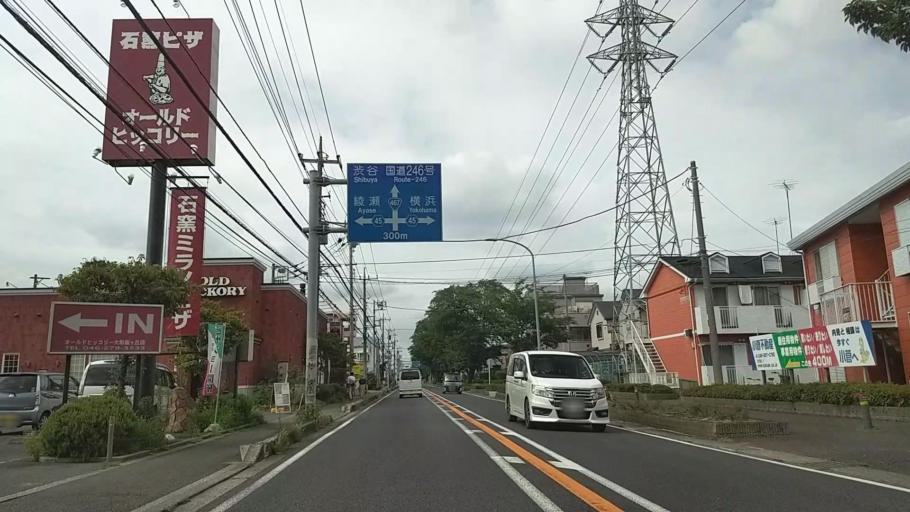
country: JP
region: Kanagawa
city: Minami-rinkan
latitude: 35.4462
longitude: 139.4674
